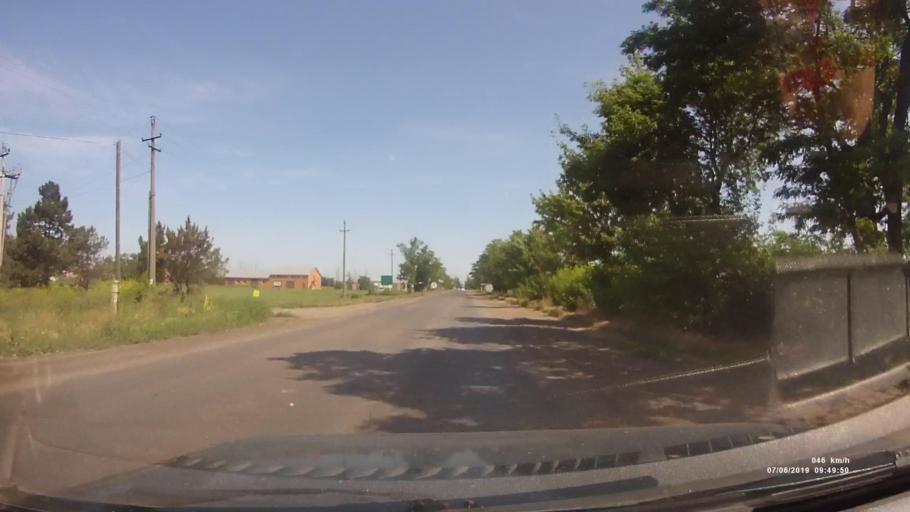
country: RU
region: Rostov
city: Azov
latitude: 47.0742
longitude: 39.4378
